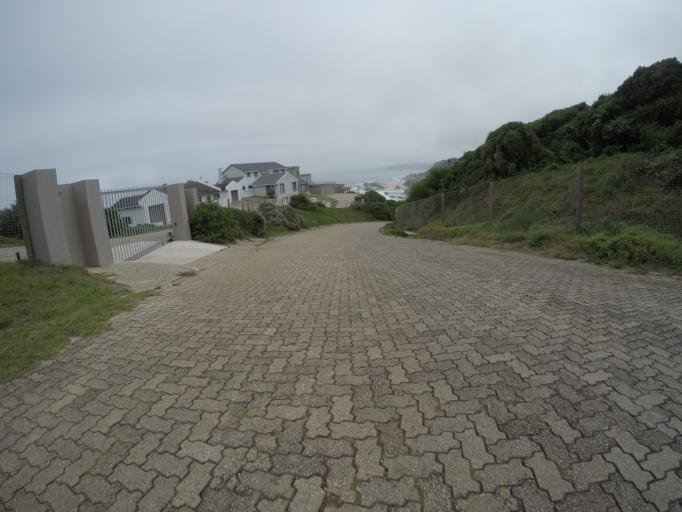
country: ZA
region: Eastern Cape
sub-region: Cacadu District Municipality
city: Kareedouw
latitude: -34.0747
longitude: 24.2321
